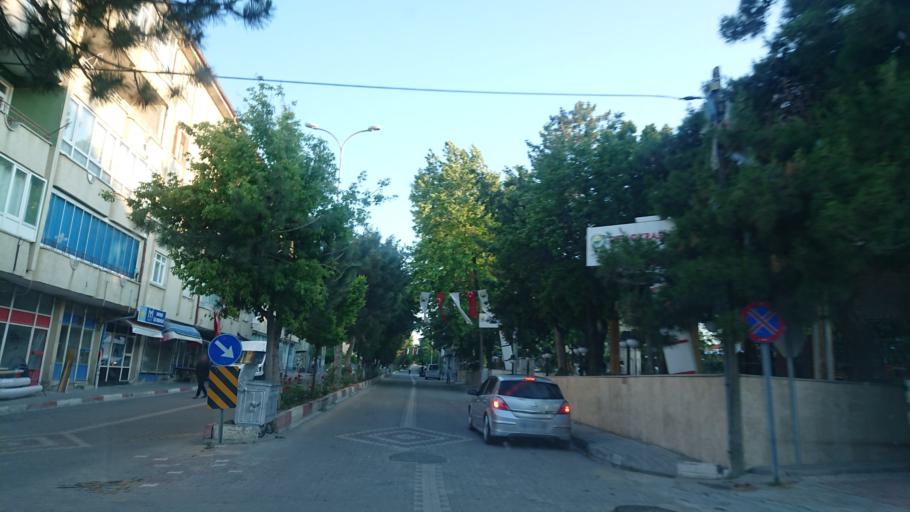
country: TR
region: Aksaray
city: Sariyahsi
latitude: 38.9825
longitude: 33.8437
